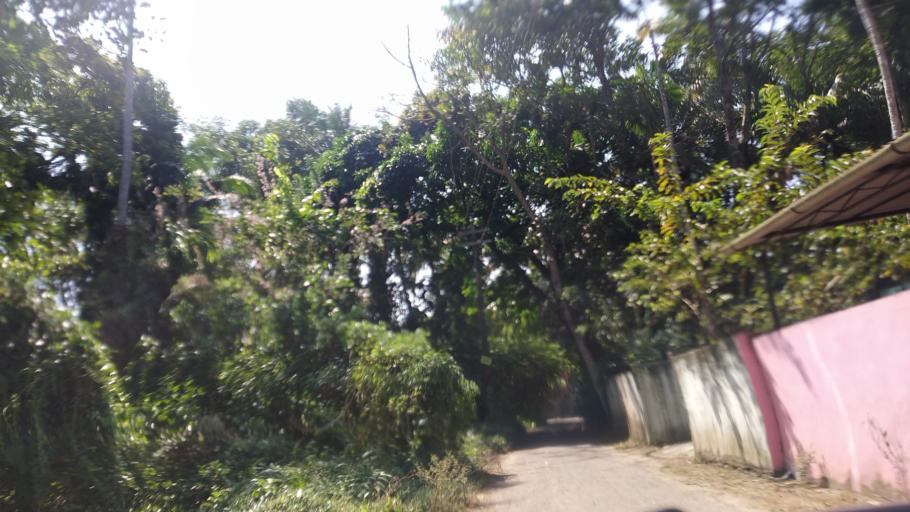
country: IN
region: Kerala
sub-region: Thrissur District
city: Kodungallur
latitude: 10.1443
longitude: 76.1953
